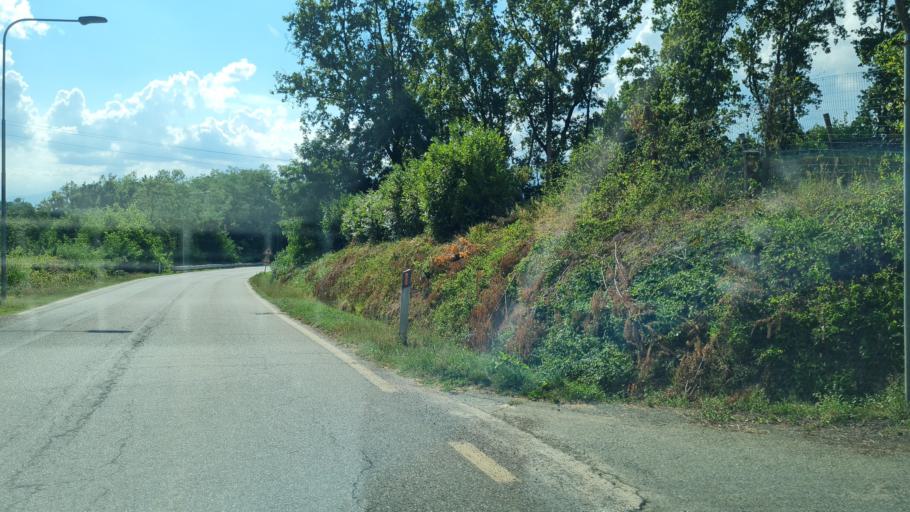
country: IT
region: Piedmont
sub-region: Provincia di Biella
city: Lessona
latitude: 45.5852
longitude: 8.2022
